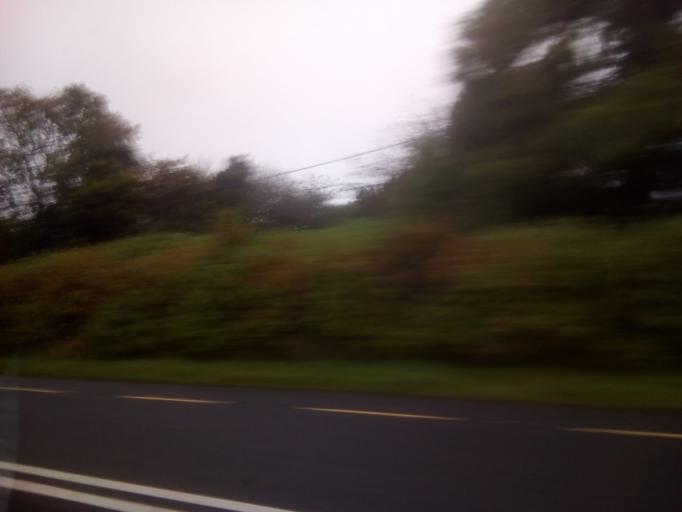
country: IE
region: Leinster
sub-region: An Iarmhi
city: An Muileann gCearr
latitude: 53.5727
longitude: -7.3636
